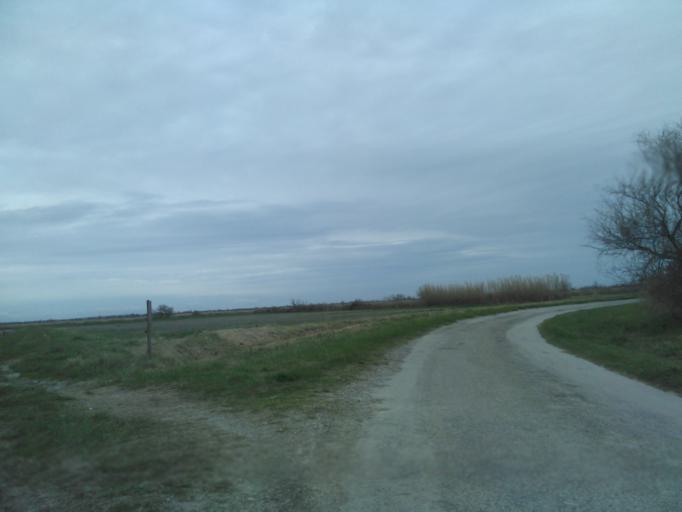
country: FR
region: Provence-Alpes-Cote d'Azur
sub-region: Departement des Bouches-du-Rhone
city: Arles
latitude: 43.5897
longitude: 4.5406
